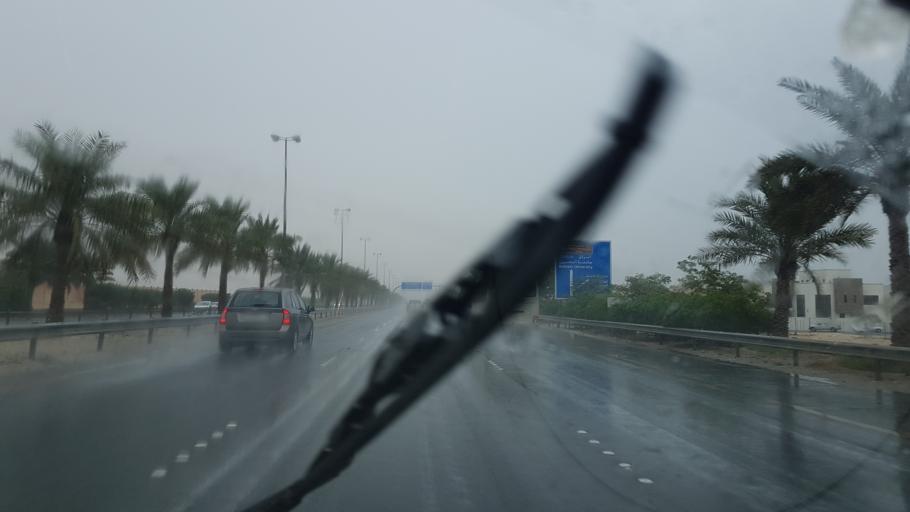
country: BH
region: Central Governorate
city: Madinat Hamad
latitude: 26.1092
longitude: 50.5111
